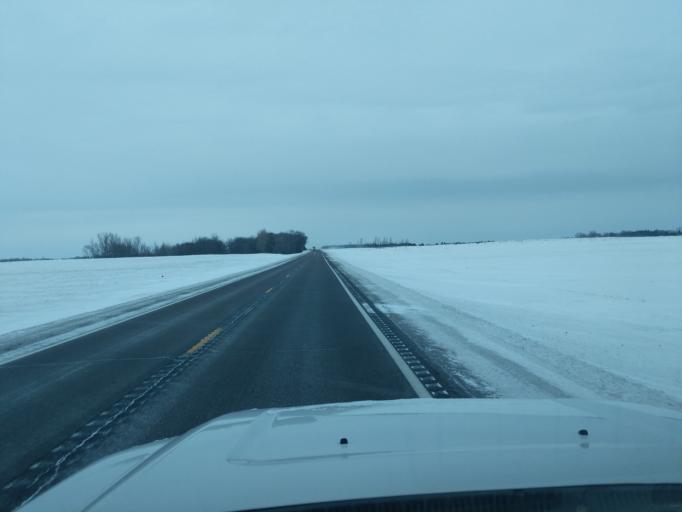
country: US
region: Minnesota
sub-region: Renville County
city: Olivia
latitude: 44.7558
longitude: -94.9953
